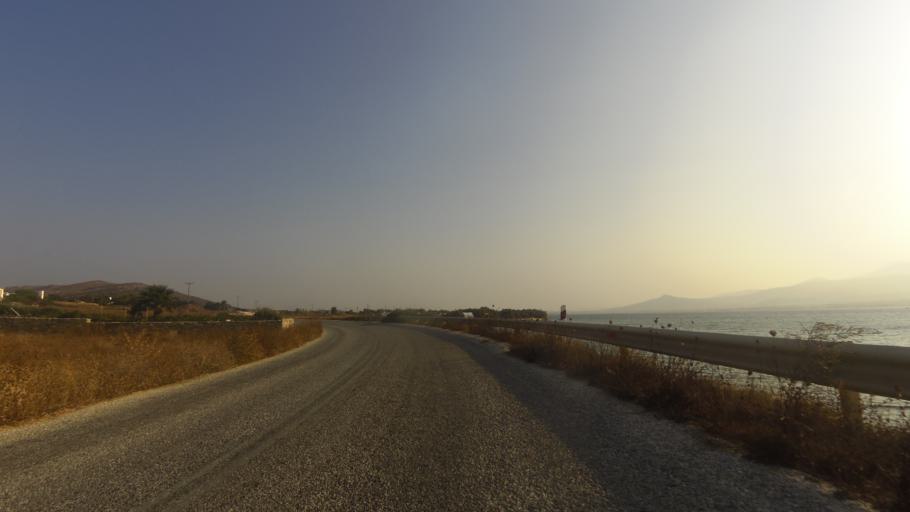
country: GR
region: South Aegean
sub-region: Nomos Kykladon
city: Antiparos
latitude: 37.0149
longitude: 25.0754
